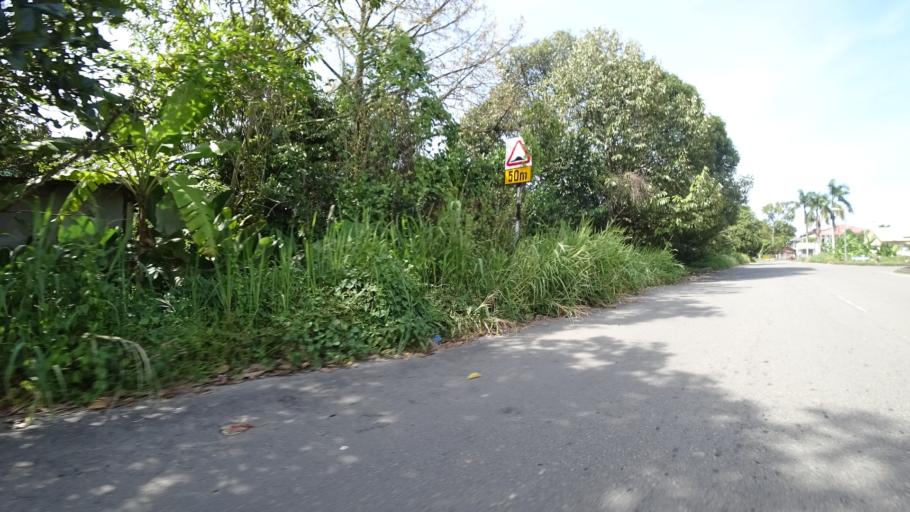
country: BN
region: Brunei and Muara
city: Bandar Seri Begawan
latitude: 4.8718
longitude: 114.8533
